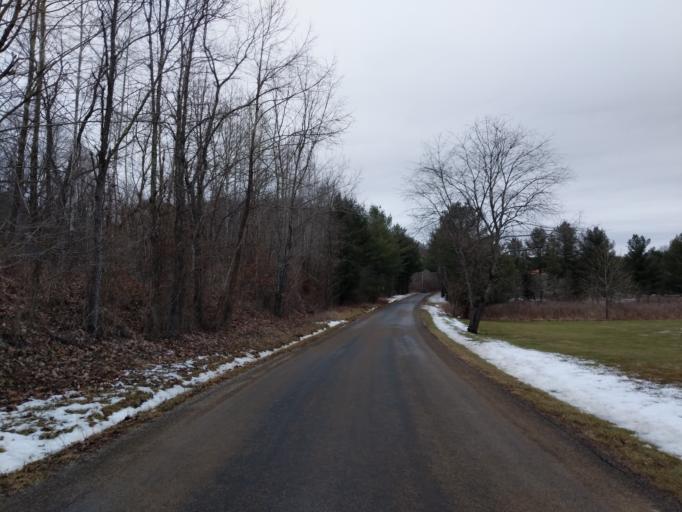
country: US
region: Ohio
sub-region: Athens County
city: The Plains
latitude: 39.3416
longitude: -82.1717
